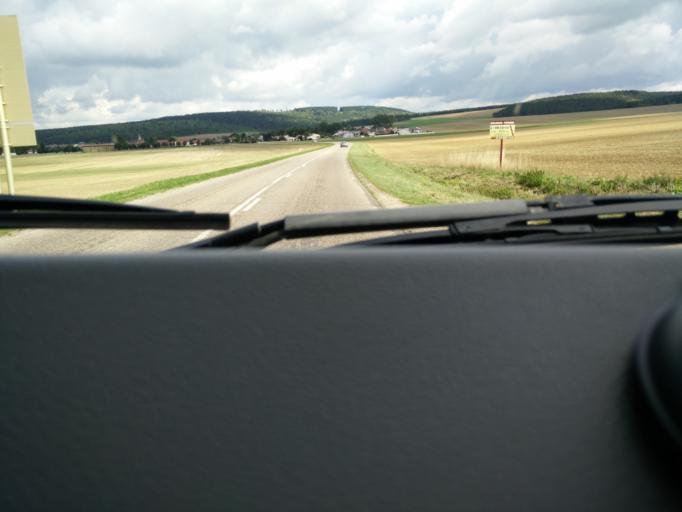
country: FR
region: Lorraine
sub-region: Departement de la Meuse
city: Belleville-sur-Meuse
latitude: 49.2003
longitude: 5.3779
